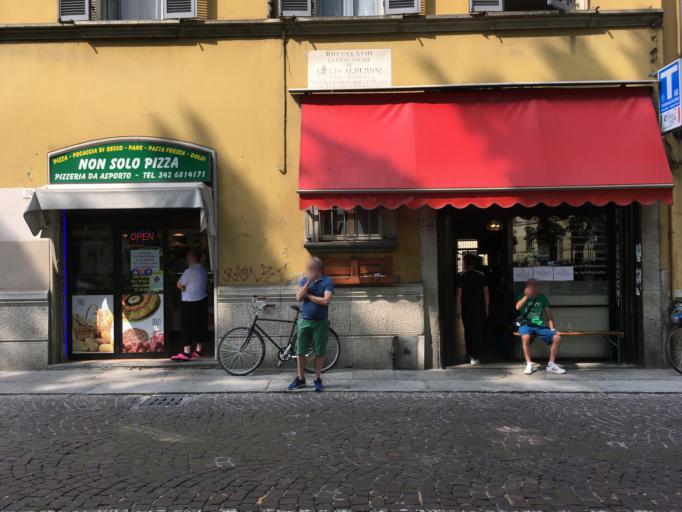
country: IT
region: Emilia-Romagna
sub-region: Provincia di Piacenza
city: Piacenza
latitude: 45.0507
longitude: 9.7012
